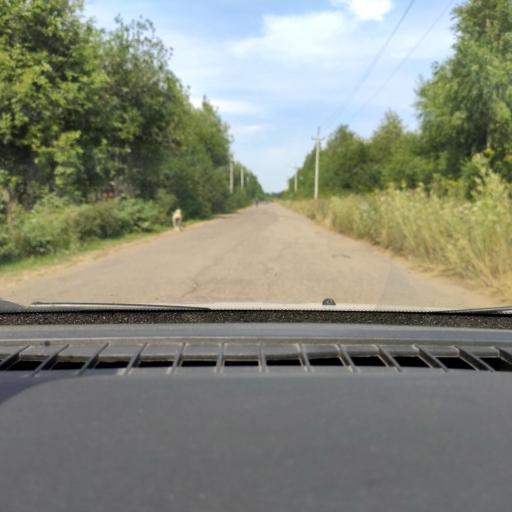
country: RU
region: Perm
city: Polazna
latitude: 58.1799
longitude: 56.4214
